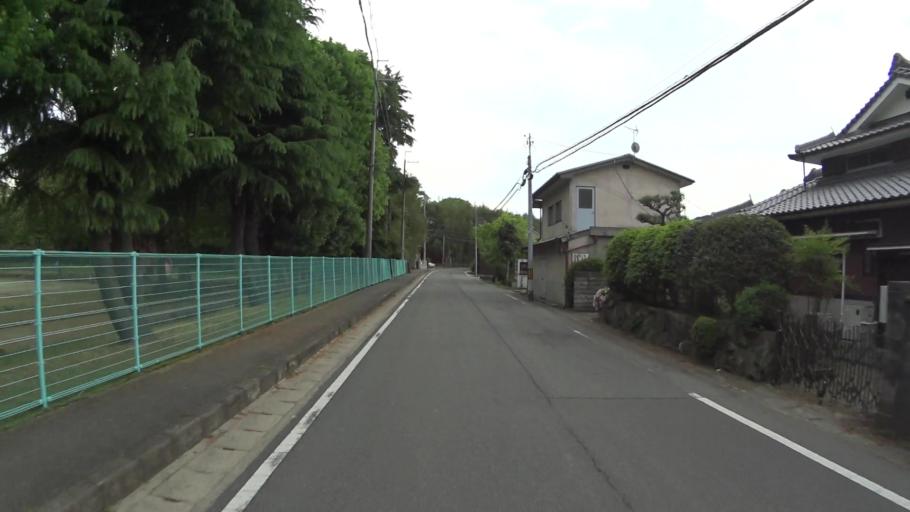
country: JP
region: Kyoto
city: Kameoka
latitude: 35.0118
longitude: 135.5481
